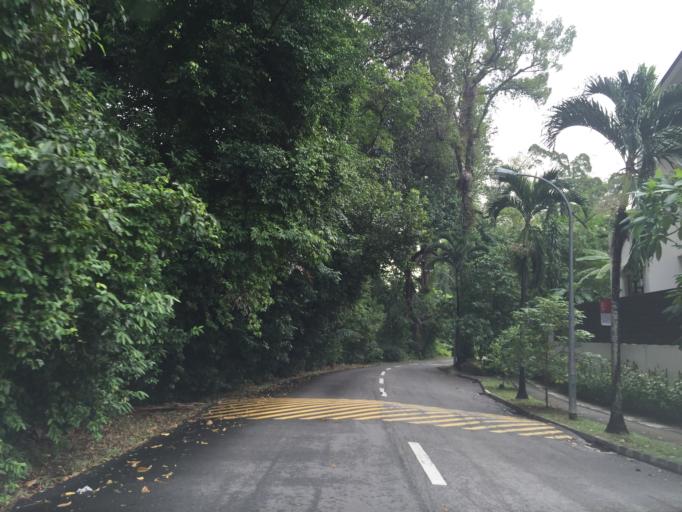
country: SG
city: Singapore
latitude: 1.3222
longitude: 103.8341
